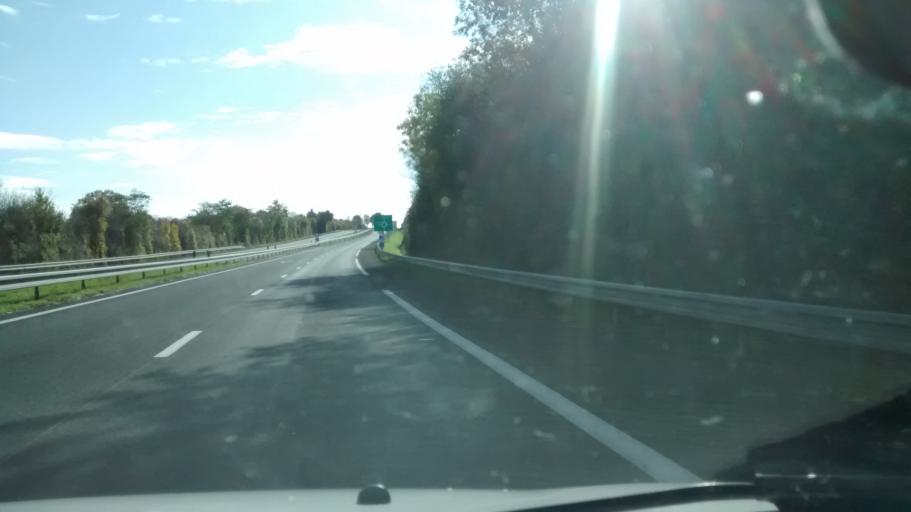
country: FR
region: Pays de la Loire
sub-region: Departement de Maine-et-Loire
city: Pouance
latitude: 47.7515
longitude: -1.1599
